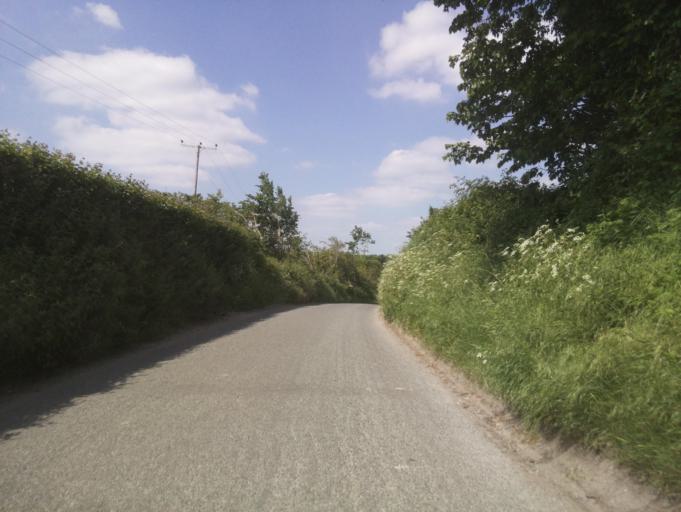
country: GB
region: England
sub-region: Wiltshire
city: Rushall
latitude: 51.2506
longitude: -1.7869
